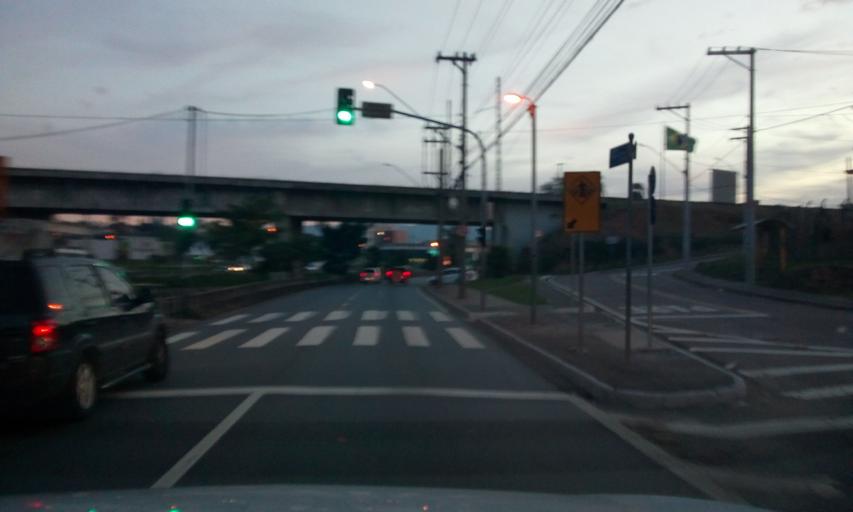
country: BR
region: Sao Paulo
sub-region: Jundiai
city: Jundiai
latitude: -23.1735
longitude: -46.8948
